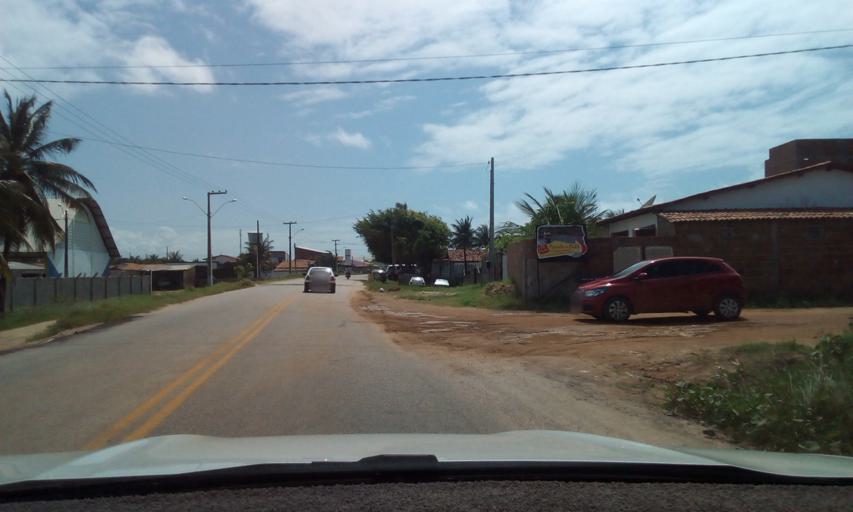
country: BR
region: Paraiba
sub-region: Rio Tinto
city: Rio Tinto
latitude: -6.7005
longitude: -34.9362
